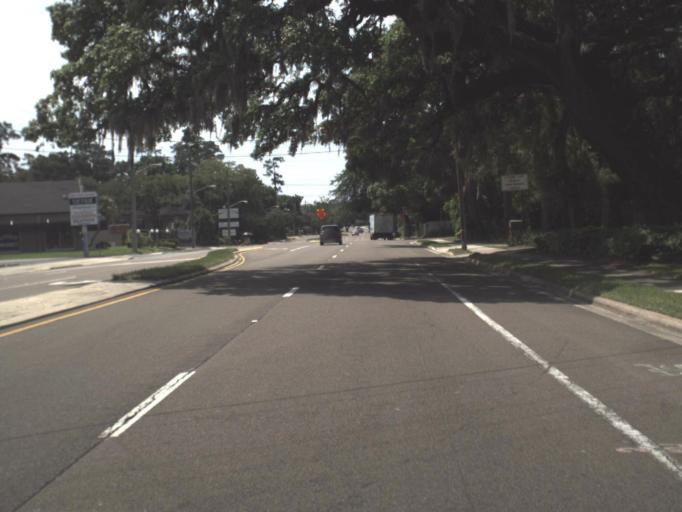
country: US
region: Florida
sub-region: Duval County
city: Jacksonville
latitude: 30.2663
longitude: -81.6479
